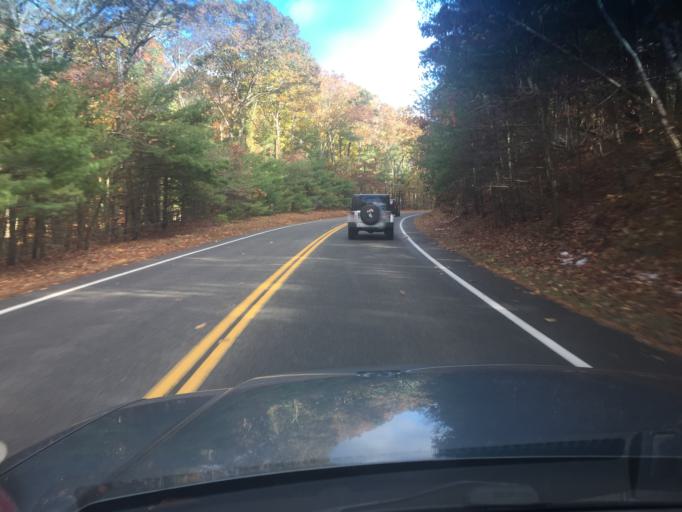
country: US
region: Massachusetts
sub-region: Norfolk County
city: Dover
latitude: 42.2253
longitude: -71.2971
